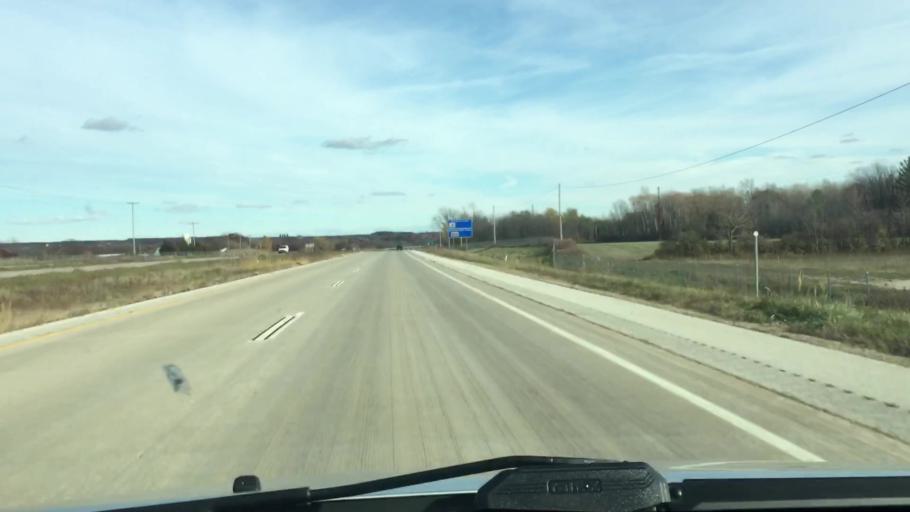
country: US
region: Wisconsin
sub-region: Kewaunee County
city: Luxemburg
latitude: 44.6338
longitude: -87.7897
